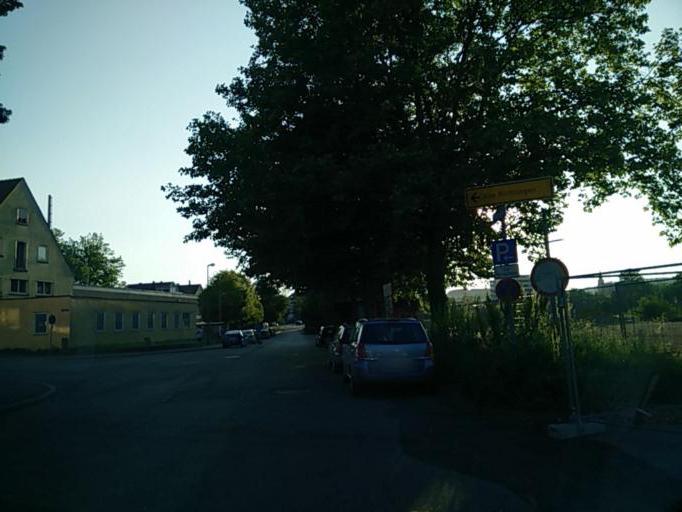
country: DE
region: Baden-Wuerttemberg
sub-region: Tuebingen Region
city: Tuebingen
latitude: 48.5155
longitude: 9.0668
